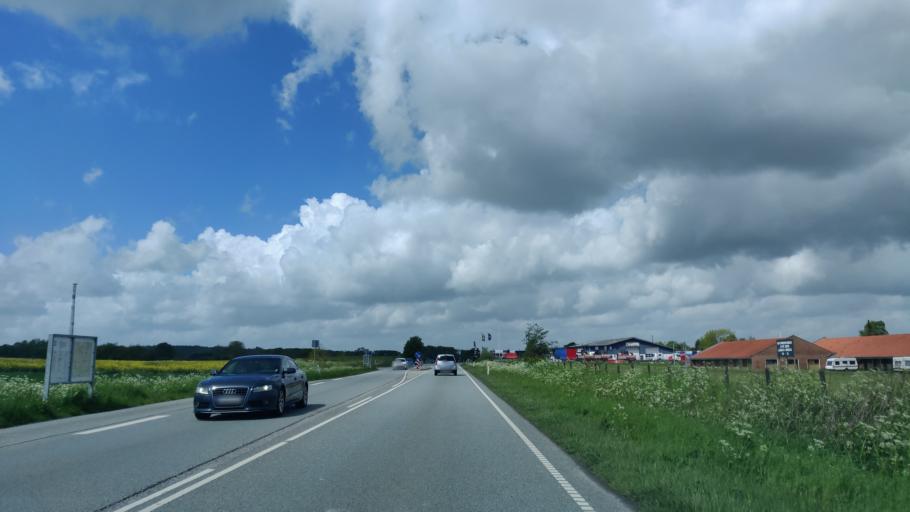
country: DK
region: Central Jutland
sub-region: Hedensted Kommune
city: Torring
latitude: 55.8440
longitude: 9.4925
